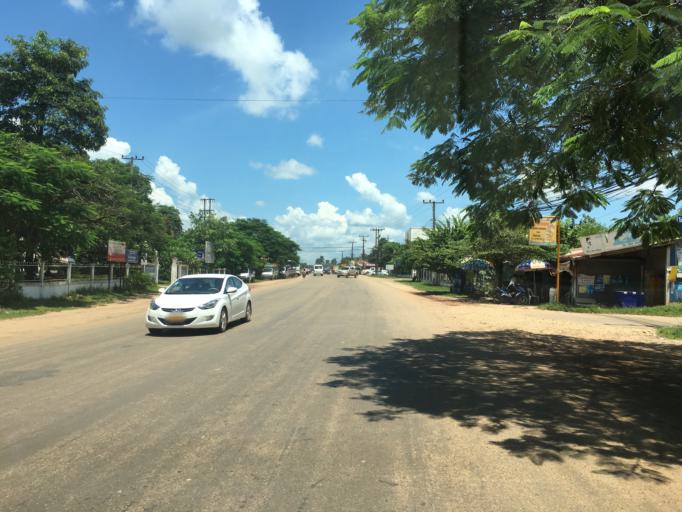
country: LA
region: Vientiane
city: Vientiane
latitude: 18.0643
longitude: 102.5380
